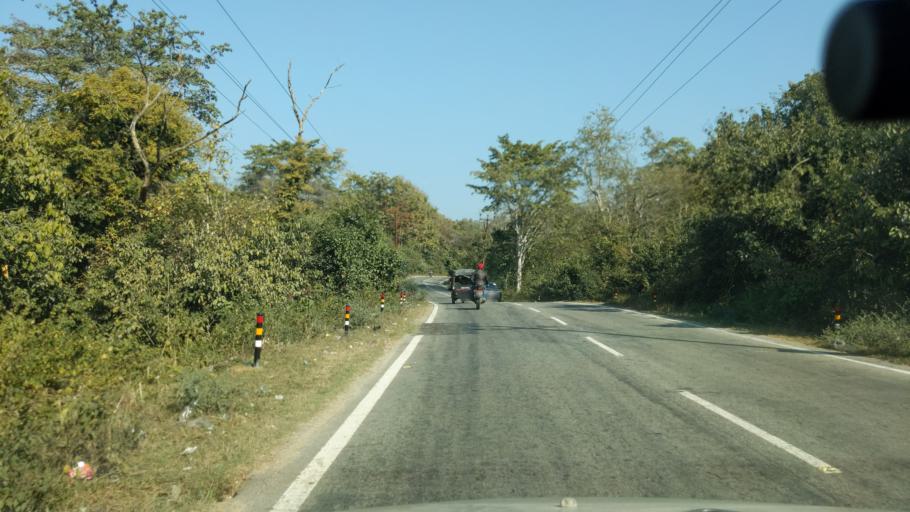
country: IN
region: Uttarakhand
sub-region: Naini Tal
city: Ramnagar
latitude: 29.3782
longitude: 79.1431
